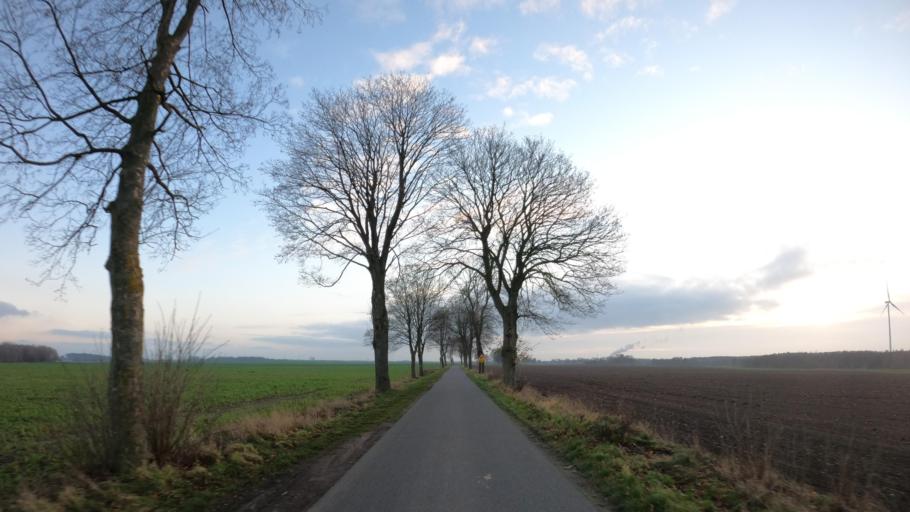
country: PL
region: West Pomeranian Voivodeship
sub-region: Powiat bialogardzki
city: Karlino
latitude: 54.0961
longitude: 15.8861
